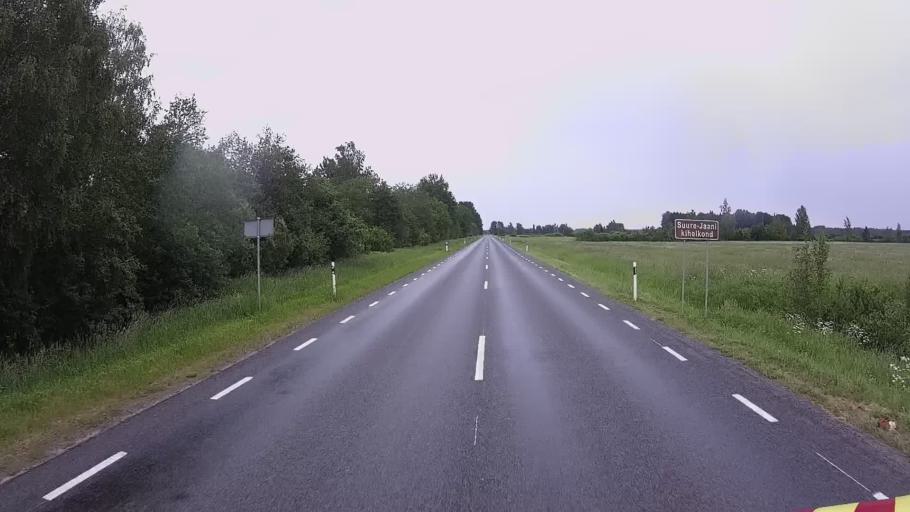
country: EE
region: Paernumaa
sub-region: Vaendra vald (alev)
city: Vandra
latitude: 58.5909
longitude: 25.1606
